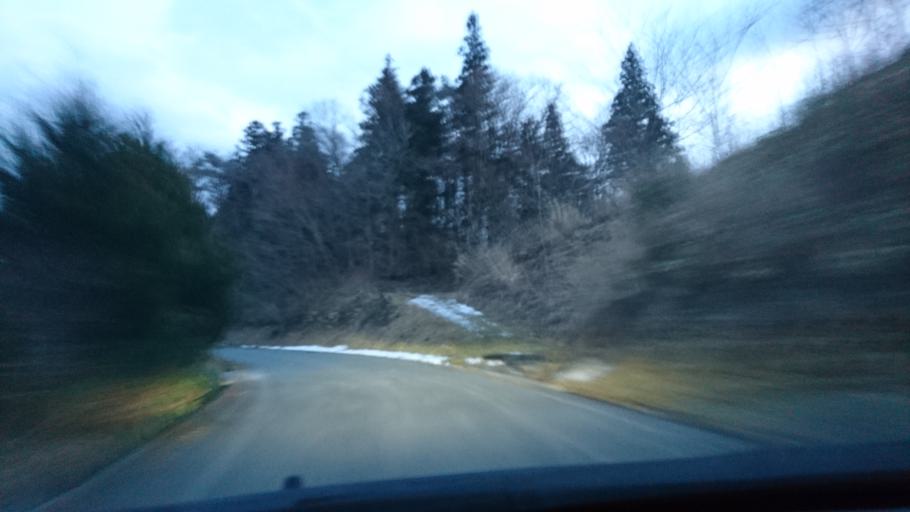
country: JP
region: Iwate
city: Ichinoseki
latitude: 38.9074
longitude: 141.3466
